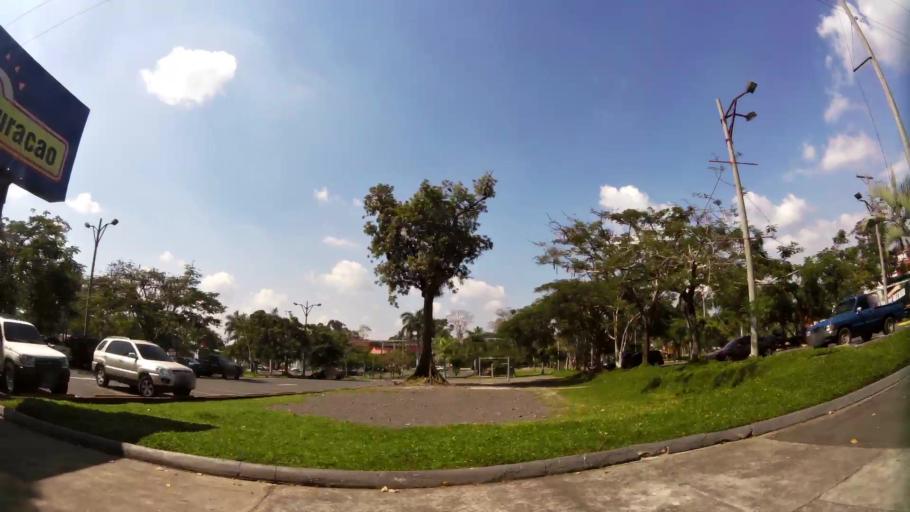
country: GT
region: Suchitepeque
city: Mazatenango
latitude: 14.5354
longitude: -91.4932
